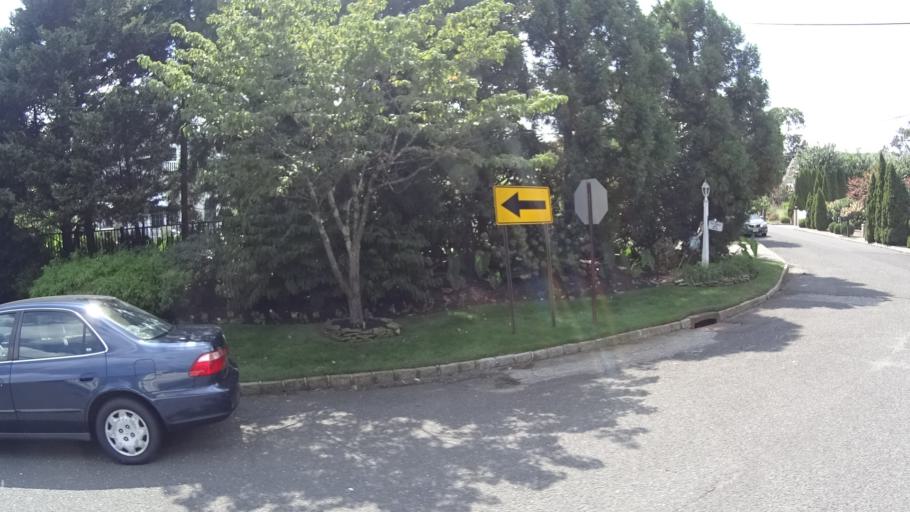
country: US
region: New Jersey
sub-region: Monmouth County
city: Brielle
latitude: 40.1088
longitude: -74.0890
